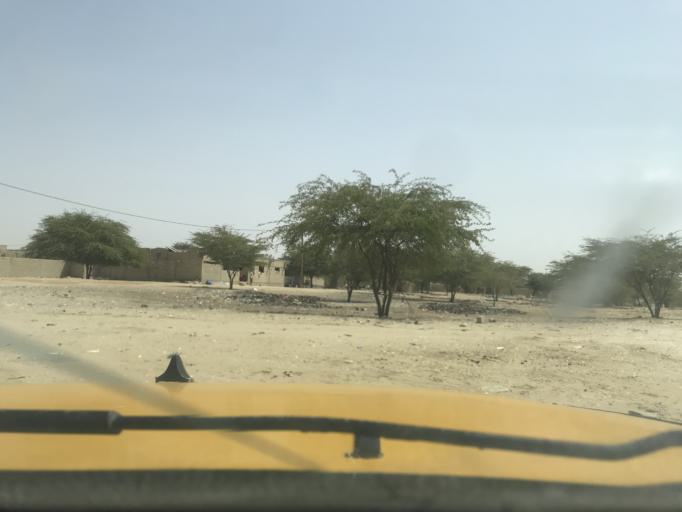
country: SN
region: Saint-Louis
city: Saint-Louis
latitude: 16.0179
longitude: -16.4474
